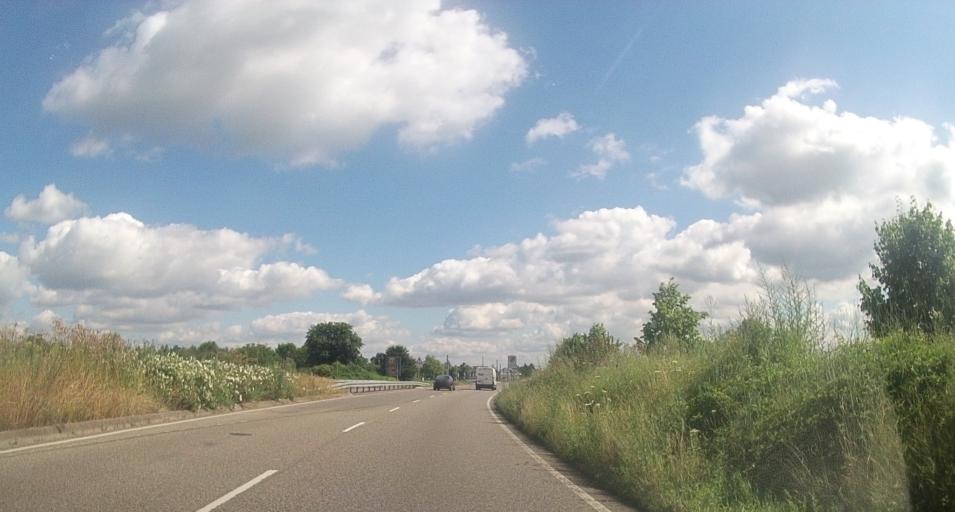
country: DE
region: Baden-Wuerttemberg
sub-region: Karlsruhe Region
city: Rheinstetten
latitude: 48.9507
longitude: 8.2889
